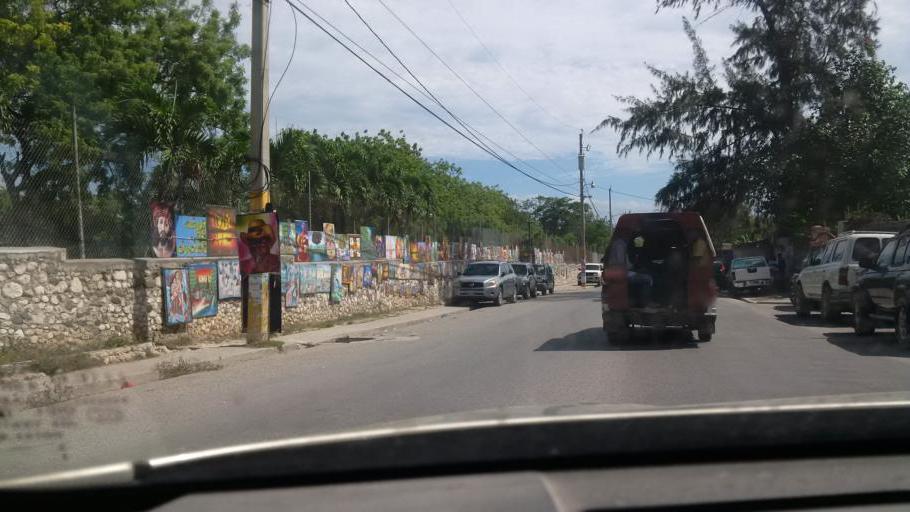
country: HT
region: Ouest
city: Delmas 73
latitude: 18.5539
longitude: -72.3016
